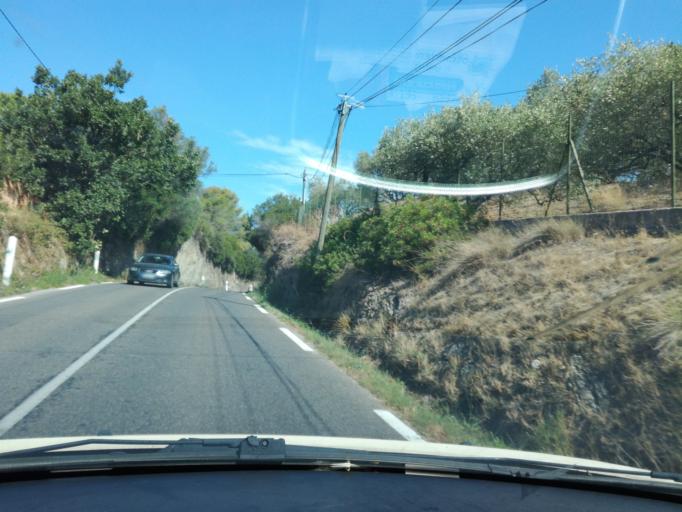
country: FR
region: Provence-Alpes-Cote d'Azur
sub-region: Departement du Var
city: La Crau
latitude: 43.1352
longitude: 6.0801
